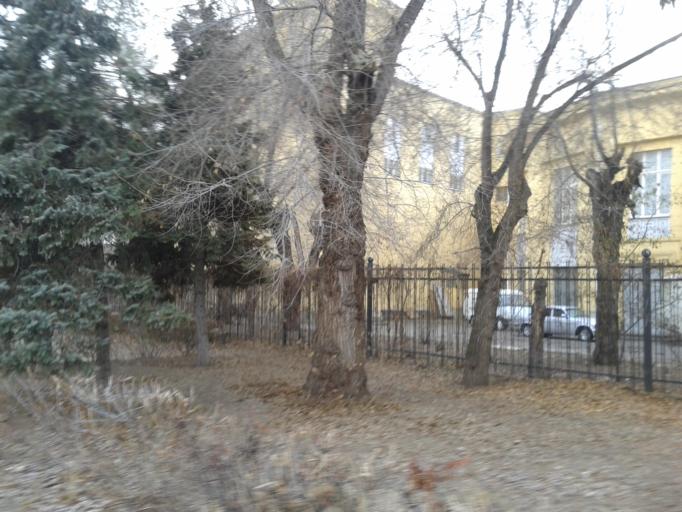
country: RU
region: Volgograd
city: Volgograd
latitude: 48.7074
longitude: 44.5109
